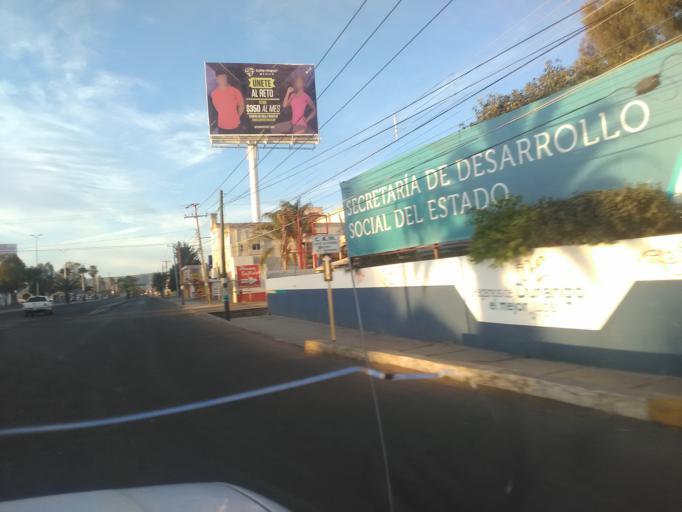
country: MX
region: Durango
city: Victoria de Durango
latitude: 23.9982
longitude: -104.6626
